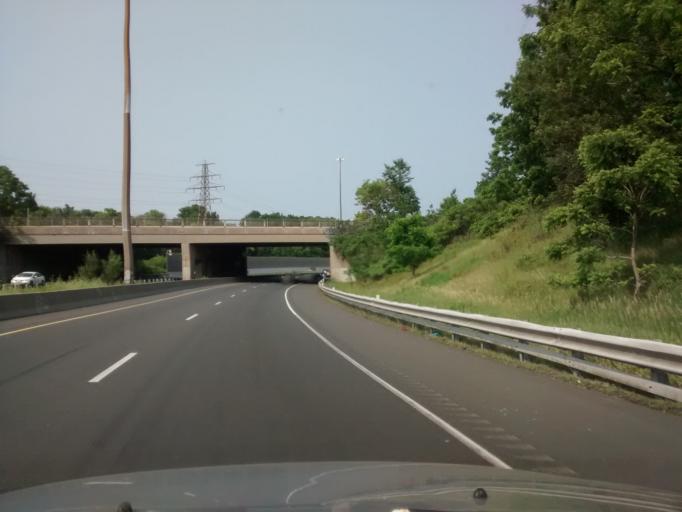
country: CA
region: Ontario
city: Hamilton
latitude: 43.2523
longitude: -79.9149
